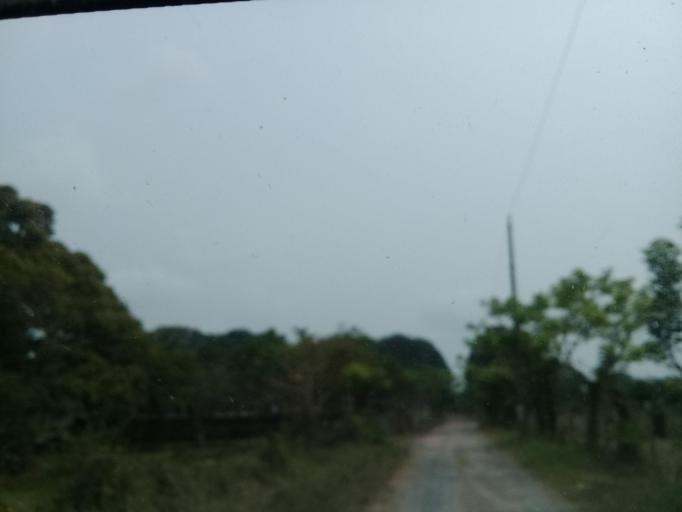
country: MX
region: Veracruz
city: El Tejar
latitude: 19.0549
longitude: -96.1921
